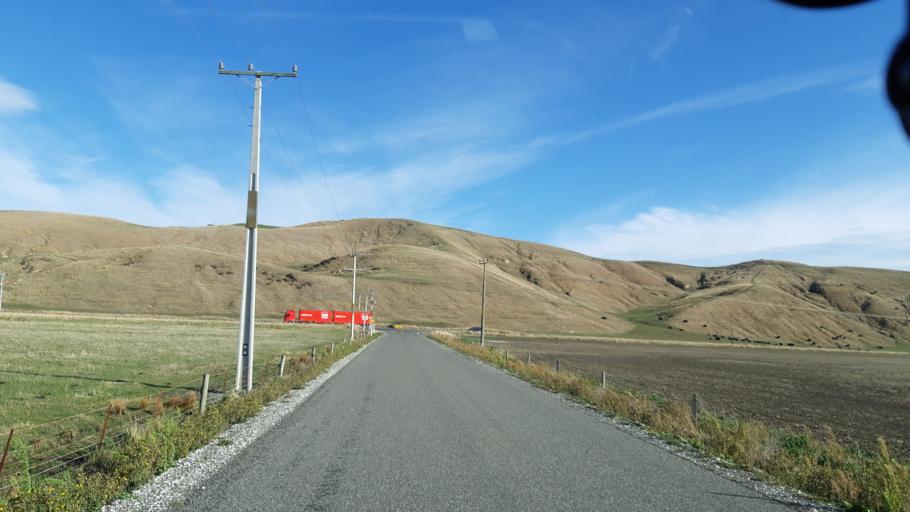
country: NZ
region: Marlborough
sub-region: Marlborough District
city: Blenheim
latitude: -41.7470
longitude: 174.1397
